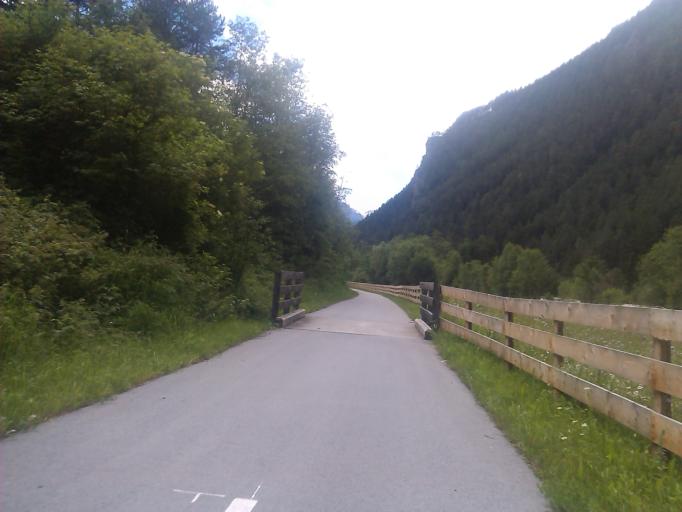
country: AT
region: Tyrol
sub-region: Politischer Bezirk Landeck
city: Fiss
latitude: 47.0408
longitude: 10.6319
